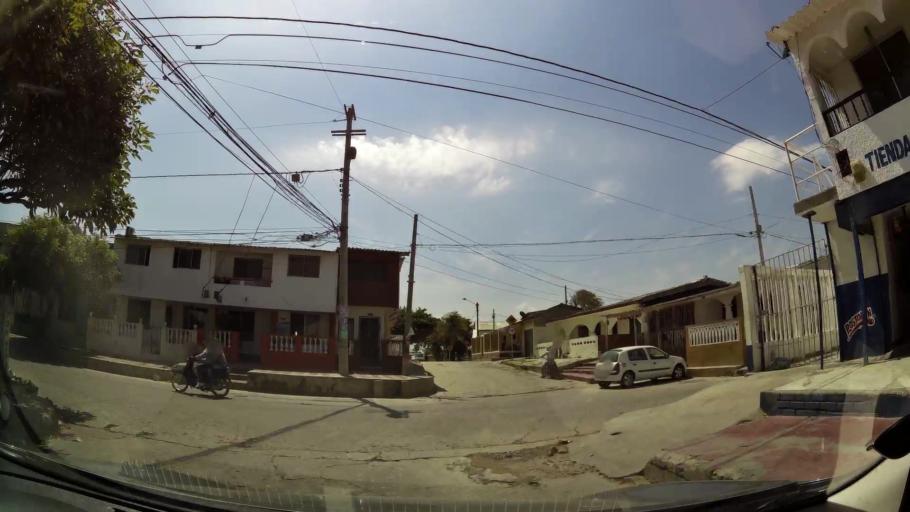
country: CO
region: Atlantico
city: Barranquilla
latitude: 10.9776
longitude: -74.8196
